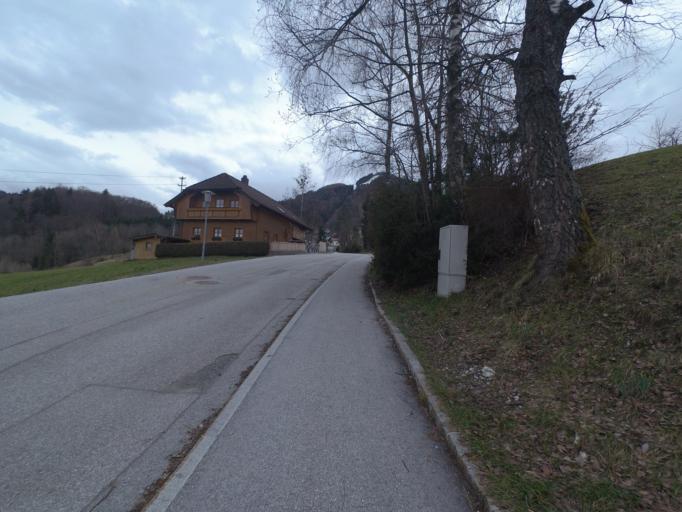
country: AT
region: Salzburg
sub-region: Politischer Bezirk Hallein
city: Hallein
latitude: 47.6635
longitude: 13.0905
